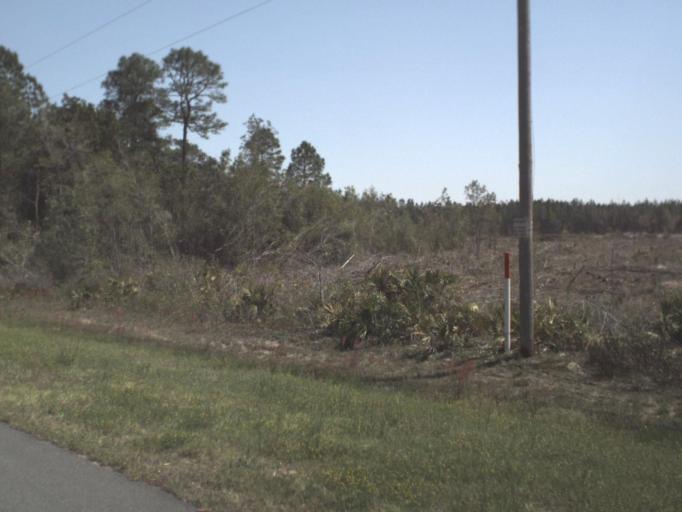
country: US
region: Florida
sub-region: Calhoun County
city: Blountstown
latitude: 30.4335
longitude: -85.2389
